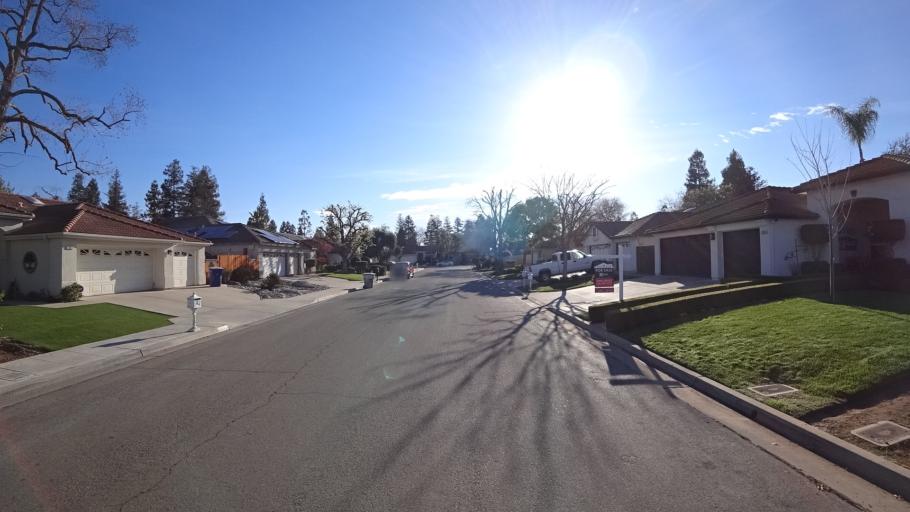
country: US
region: California
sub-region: Fresno County
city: West Park
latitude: 36.8259
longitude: -119.8601
